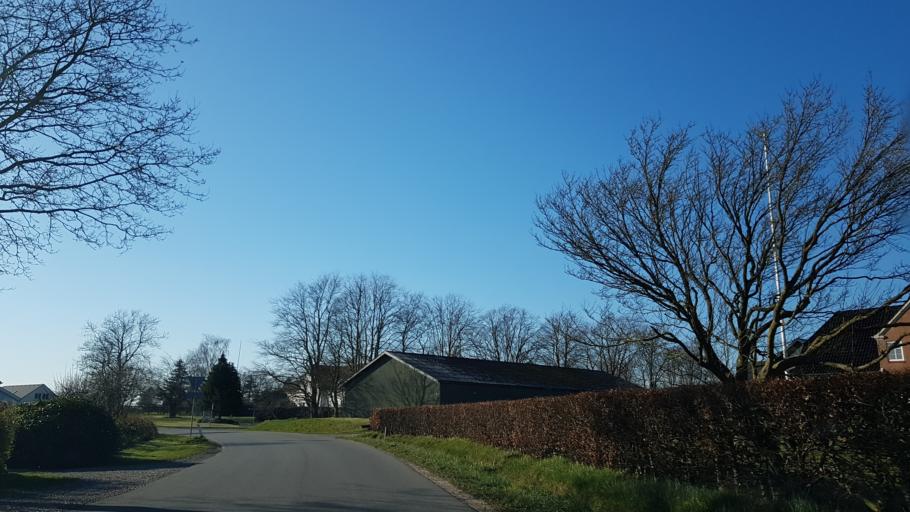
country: DK
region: South Denmark
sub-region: Vejen Kommune
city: Rodding
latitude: 55.3851
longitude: 8.9804
